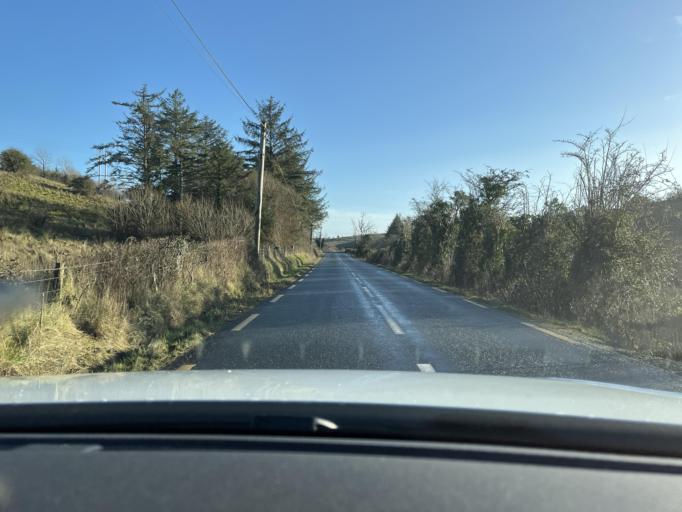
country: IE
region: Connaught
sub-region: County Leitrim
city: Manorhamilton
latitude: 54.2378
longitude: -8.2160
